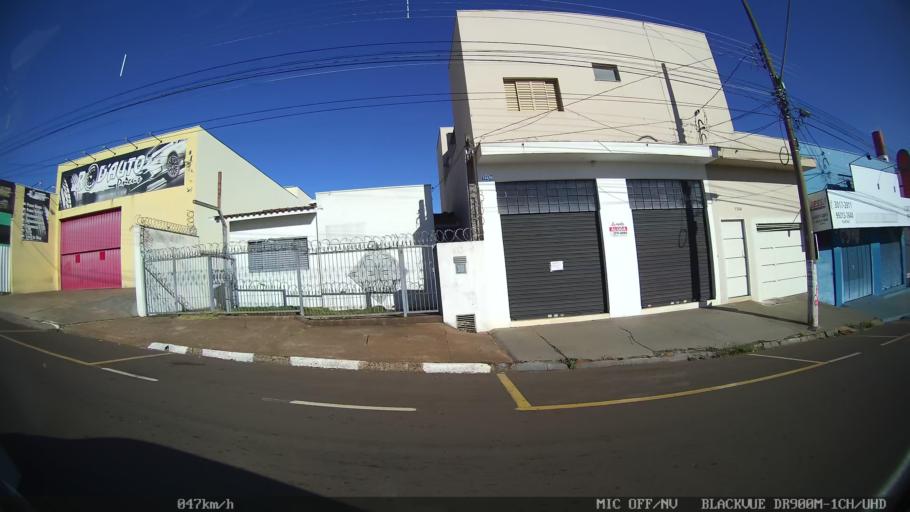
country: BR
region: Sao Paulo
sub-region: Franca
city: Franca
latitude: -20.5562
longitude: -47.3963
